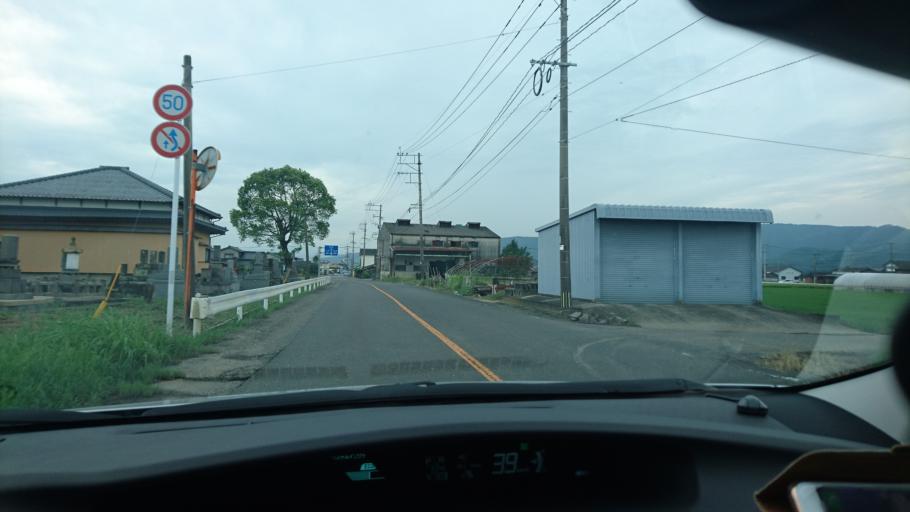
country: JP
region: Saga Prefecture
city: Kashima
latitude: 33.1965
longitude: 130.1147
